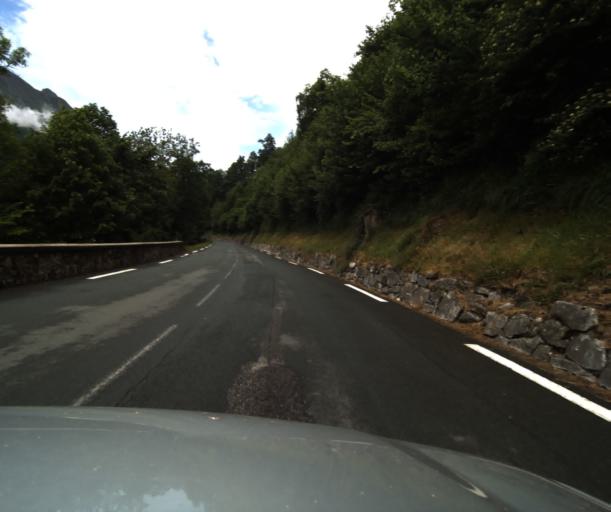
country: FR
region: Midi-Pyrenees
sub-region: Departement des Hautes-Pyrenees
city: Luz-Saint-Sauveur
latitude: 42.7932
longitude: 0.0192
